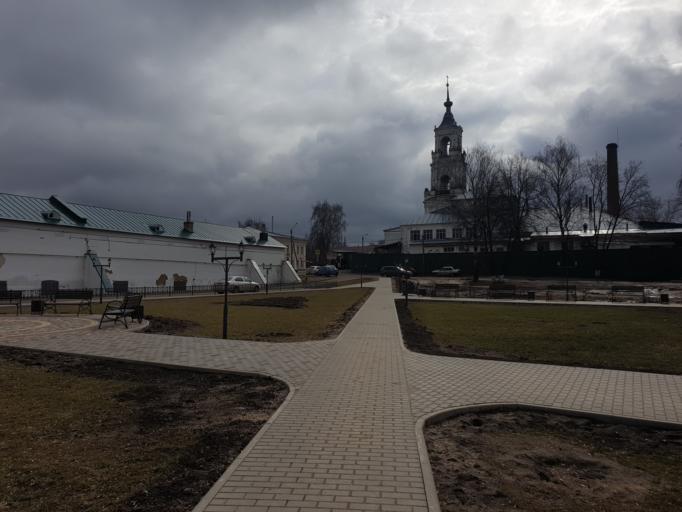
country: RU
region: Kostroma
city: Nerekhta
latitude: 57.4607
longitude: 40.5715
